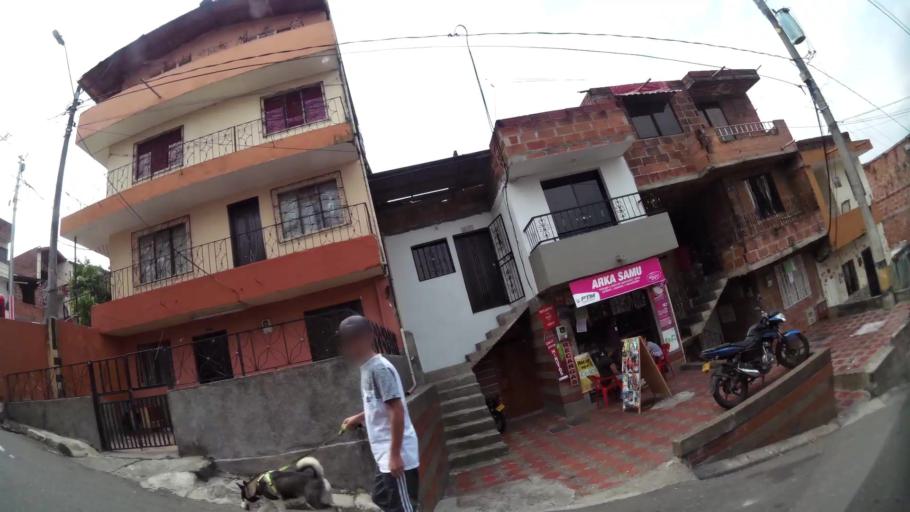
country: CO
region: Antioquia
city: Medellin
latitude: 6.2731
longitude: -75.5509
